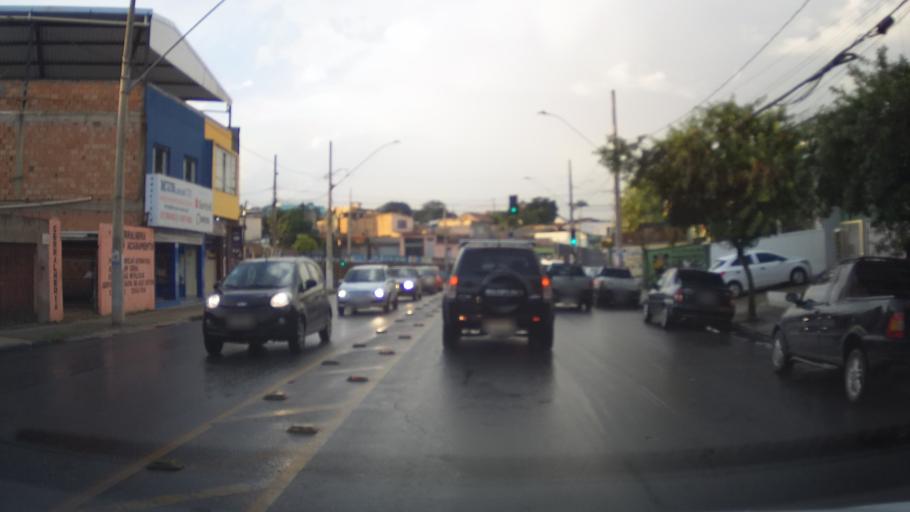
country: BR
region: Minas Gerais
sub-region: Belo Horizonte
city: Belo Horizonte
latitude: -19.9562
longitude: -43.9862
